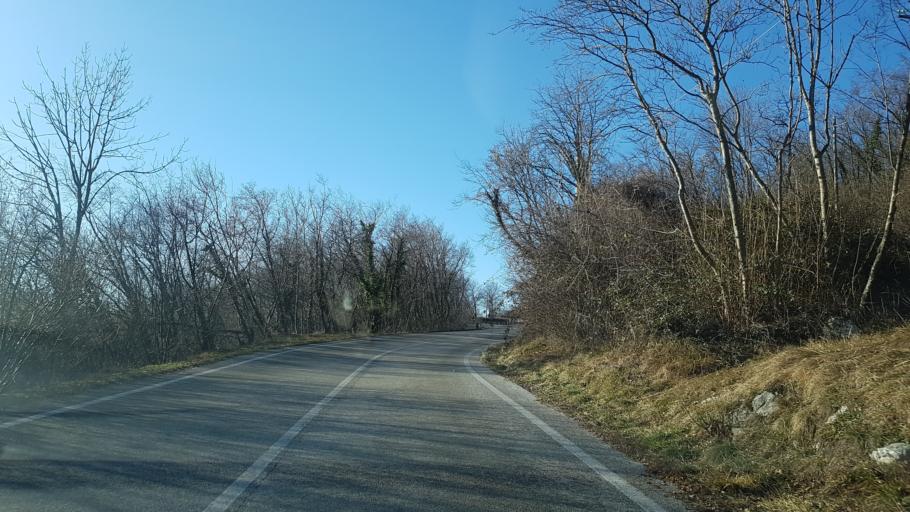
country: IT
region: Friuli Venezia Giulia
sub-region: Provincia di Udine
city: Forgaria nel Friuli
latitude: 46.2327
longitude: 12.9949
